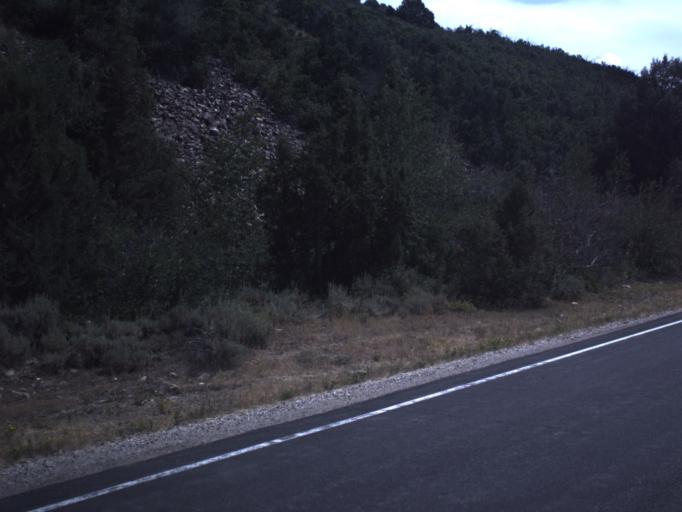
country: US
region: Utah
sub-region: Summit County
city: Francis
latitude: 40.5607
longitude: -111.1817
